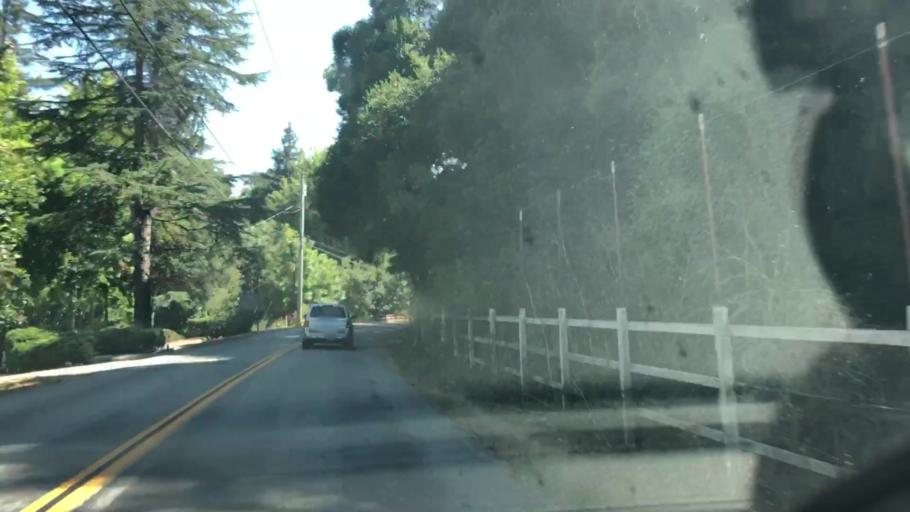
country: US
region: California
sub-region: Santa Cruz County
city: Corralitos
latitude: 37.0017
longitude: -121.8064
